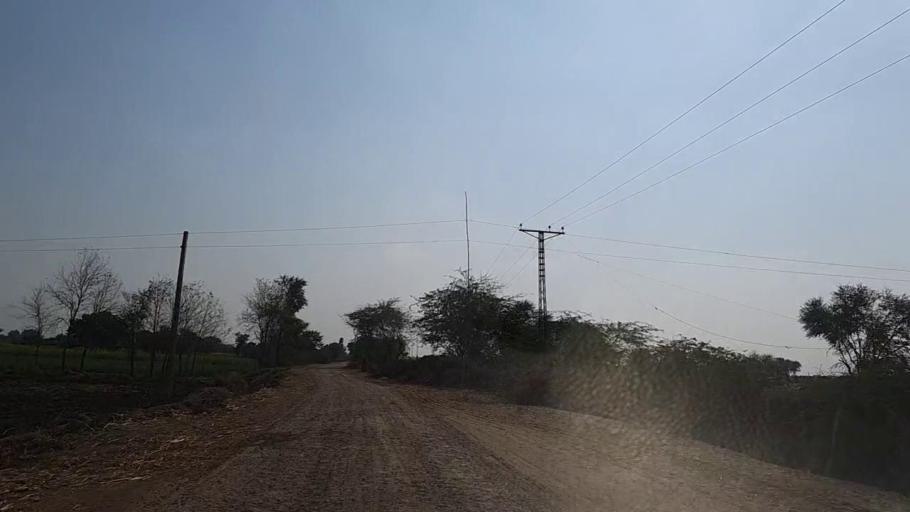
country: PK
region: Sindh
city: Daur
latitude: 26.4517
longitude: 68.2346
